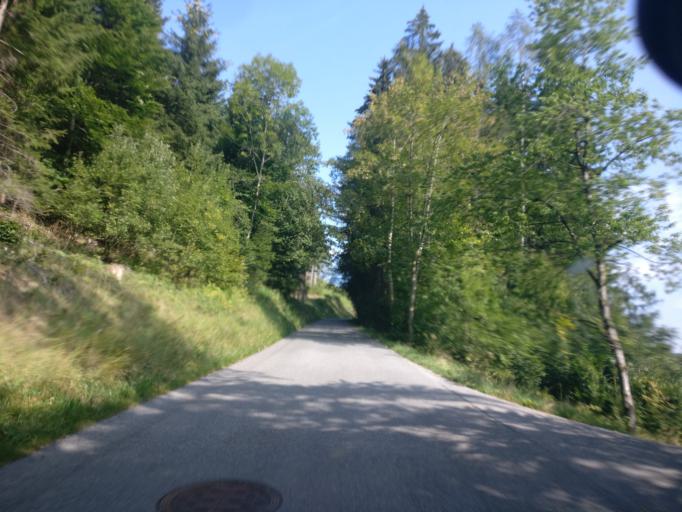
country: AT
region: Salzburg
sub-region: Politischer Bezirk Sankt Johann im Pongau
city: Pfarrwerfen
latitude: 47.4646
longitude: 13.2116
